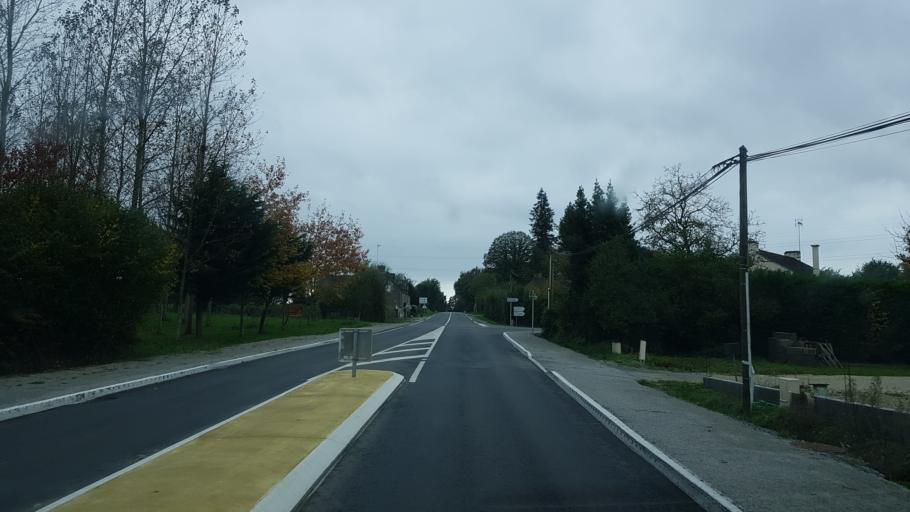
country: FR
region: Brittany
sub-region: Departement du Morbihan
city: Serent
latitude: 47.7824
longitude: -2.5172
